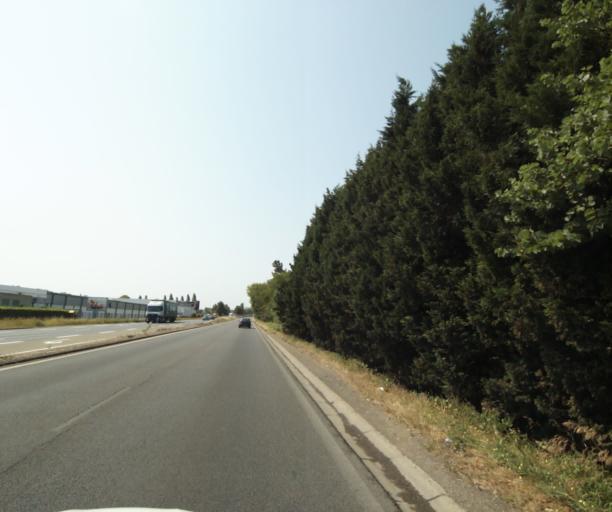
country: FR
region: Ile-de-France
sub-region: Departement du Val-d'Oise
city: Eragny
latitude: 49.0131
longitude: 2.0896
